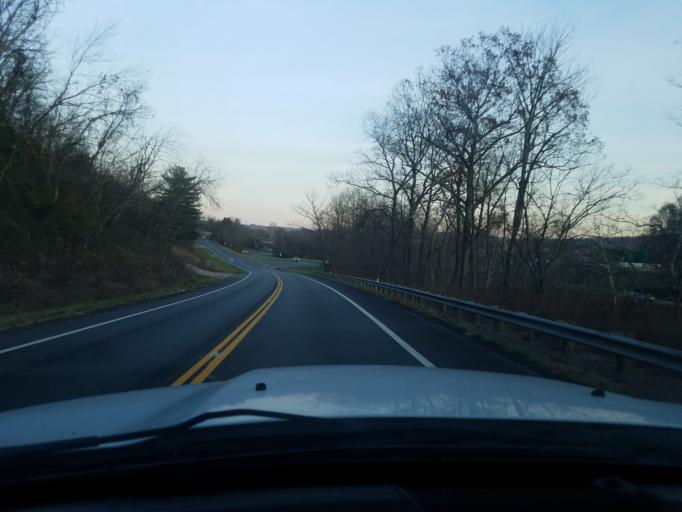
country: US
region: Ohio
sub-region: Washington County
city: Marietta
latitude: 39.4045
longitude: -81.4752
